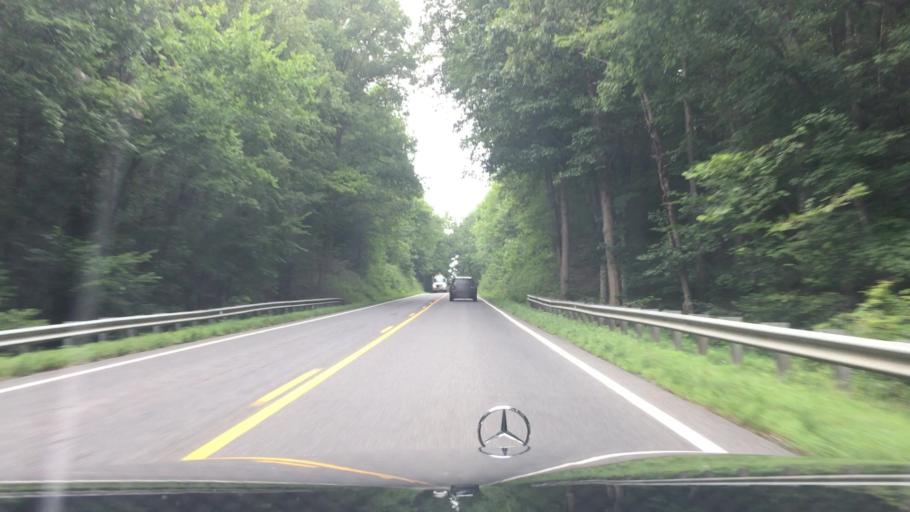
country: US
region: Virginia
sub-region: Nottoway County
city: Crewe
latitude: 37.2750
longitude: -78.1736
